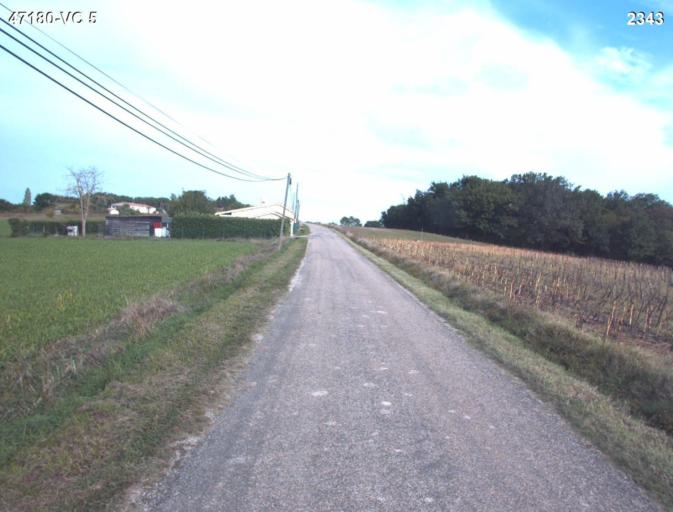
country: FR
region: Aquitaine
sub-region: Departement du Lot-et-Garonne
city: Sainte-Colombe-en-Bruilhois
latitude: 44.1640
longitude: 0.4732
